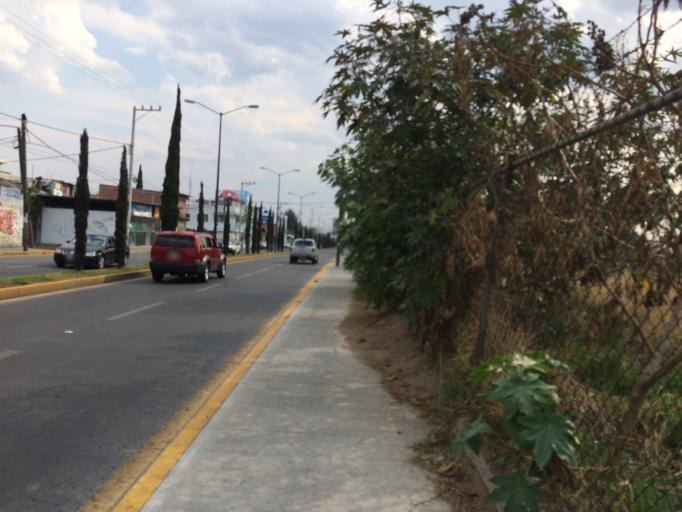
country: MX
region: Michoacan
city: Morelia
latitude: 19.6940
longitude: -101.2212
